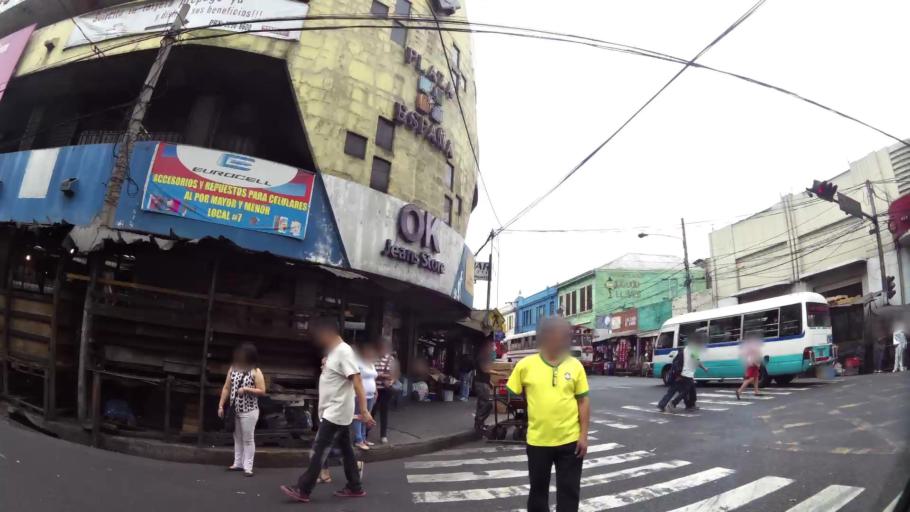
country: SV
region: San Salvador
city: San Salvador
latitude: 13.6998
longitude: -89.1913
